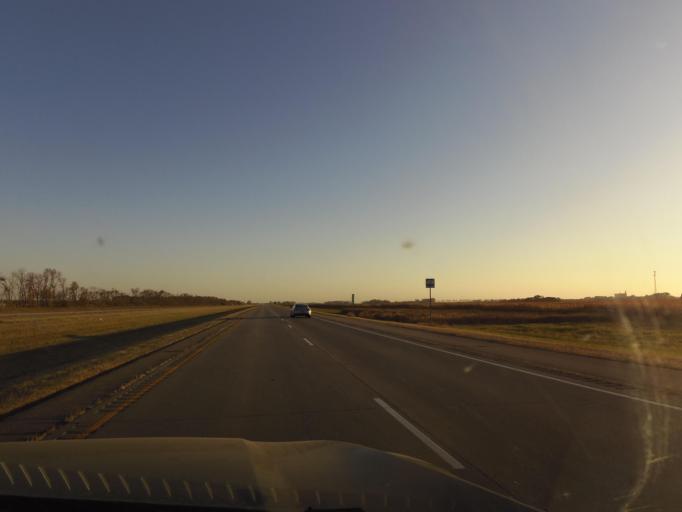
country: US
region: North Dakota
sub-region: Grand Forks County
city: Grand Forks
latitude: 47.8027
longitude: -97.0779
